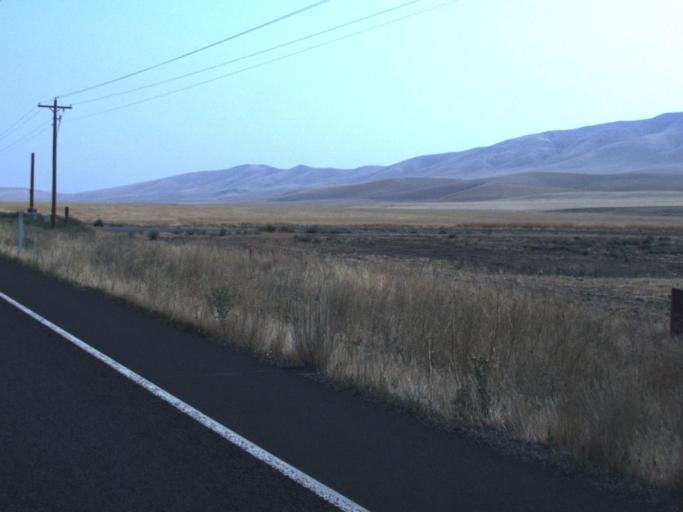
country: US
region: Washington
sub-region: Yakima County
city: Sunnyside
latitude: 46.5144
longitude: -120.0416
